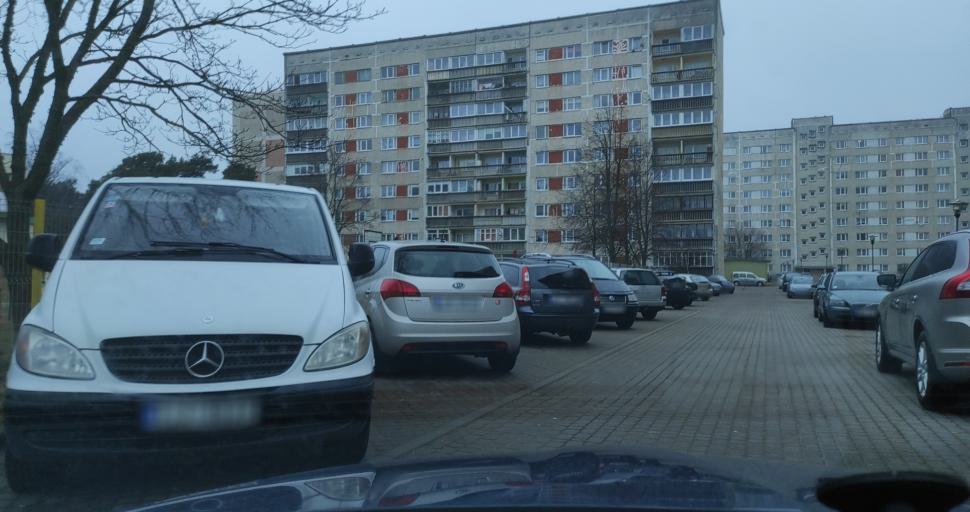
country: LV
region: Ventspils
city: Ventspils
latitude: 57.3831
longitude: 21.5485
